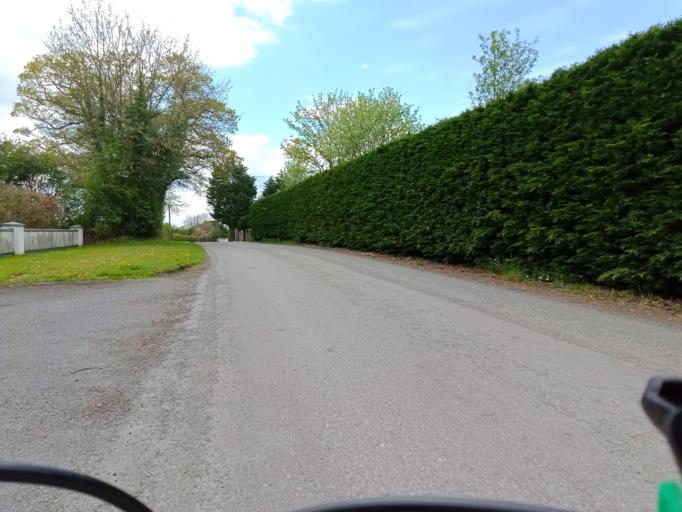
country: IE
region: Leinster
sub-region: Kilkenny
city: Kilkenny
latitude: 52.6311
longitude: -7.2855
